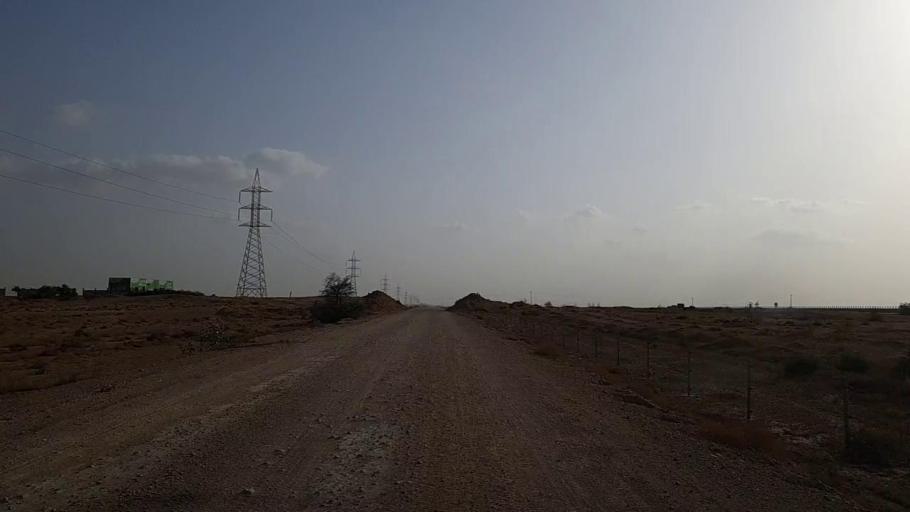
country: PK
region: Sindh
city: Kotri
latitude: 25.2080
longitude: 67.8936
